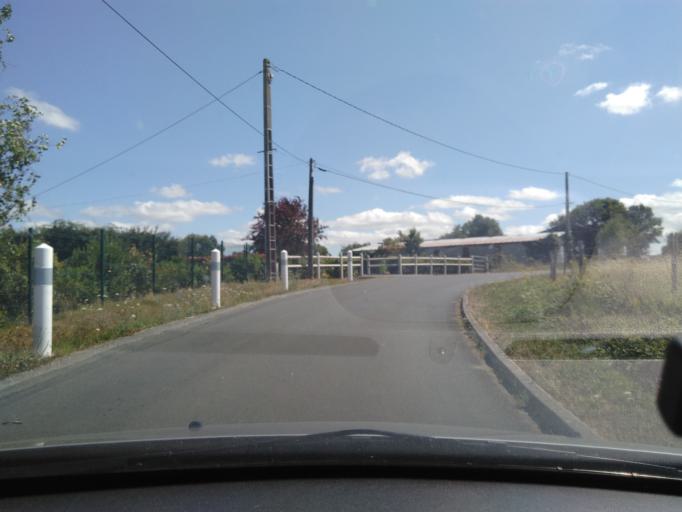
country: FR
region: Pays de la Loire
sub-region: Departement de la Vendee
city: Dompierre-sur-Yon
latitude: 46.7157
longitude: -1.3968
